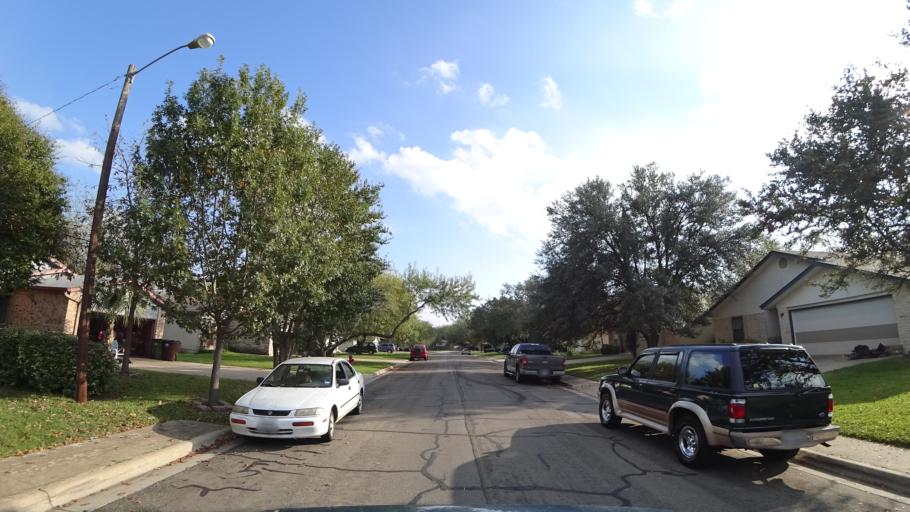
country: US
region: Texas
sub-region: Williamson County
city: Round Rock
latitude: 30.4903
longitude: -97.6645
